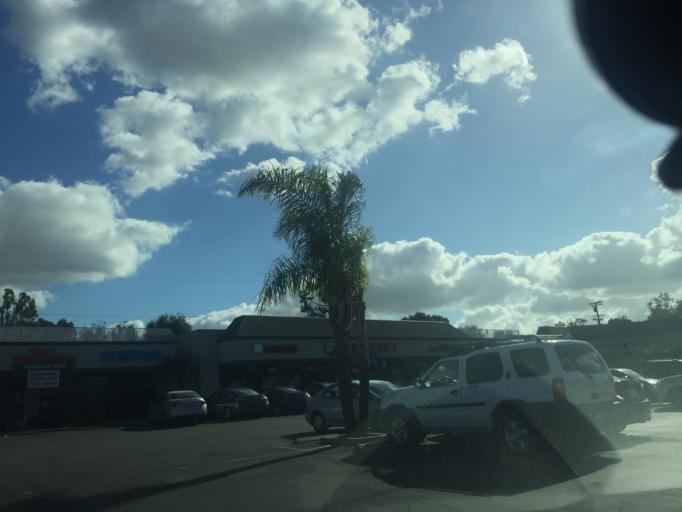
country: US
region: California
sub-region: San Diego County
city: La Mesa
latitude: 32.7875
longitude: -117.0975
